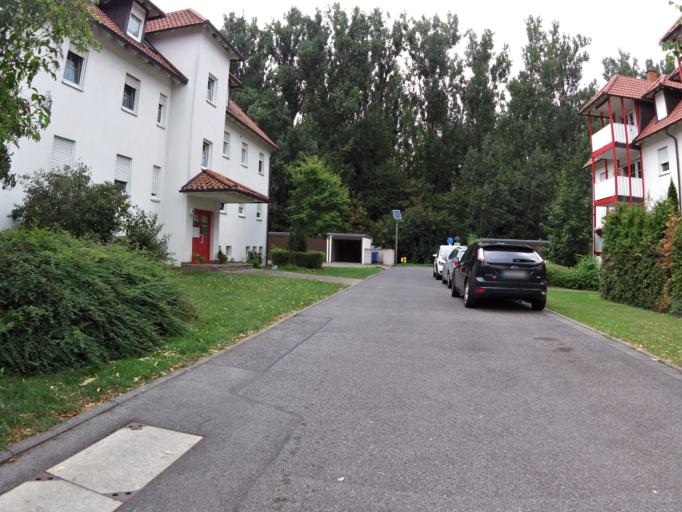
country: DE
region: Bavaria
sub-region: Regierungsbezirk Unterfranken
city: Sand
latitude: 49.9843
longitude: 10.6262
